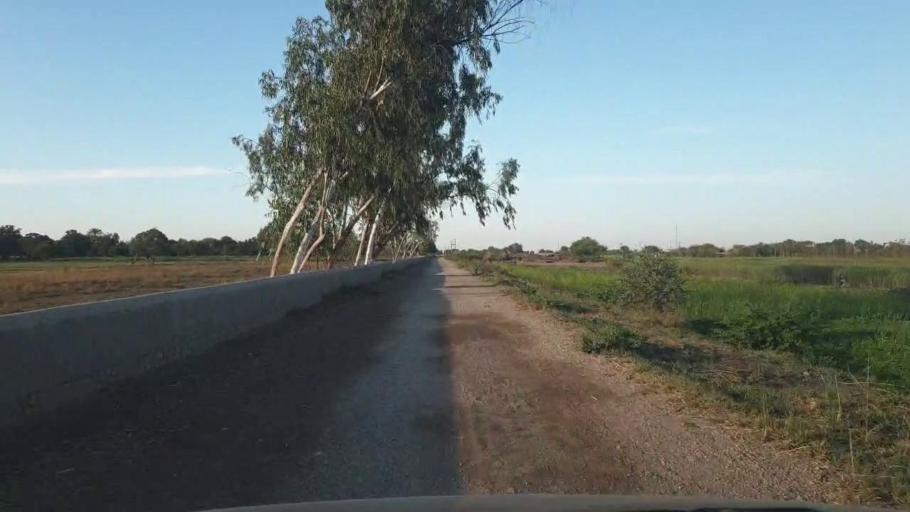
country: PK
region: Sindh
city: Dhoro Naro
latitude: 25.3935
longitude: 69.5756
